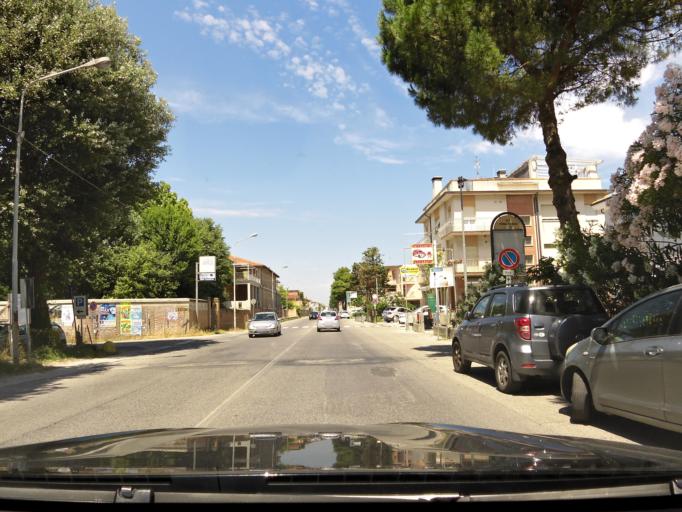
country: IT
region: The Marches
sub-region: Provincia di Ancona
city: Senigallia
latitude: 43.7255
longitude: 13.2055
